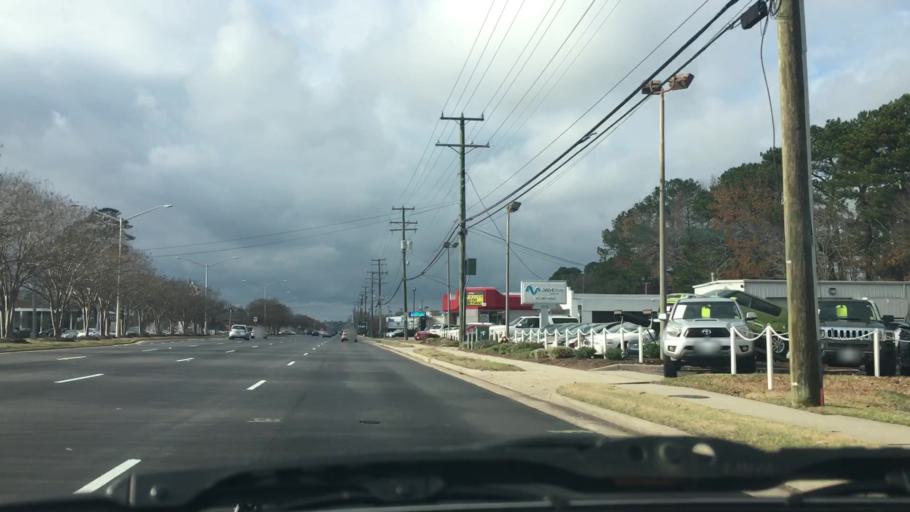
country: US
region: Virginia
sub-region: City of Chesapeake
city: Chesapeake
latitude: 36.8471
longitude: -76.1597
